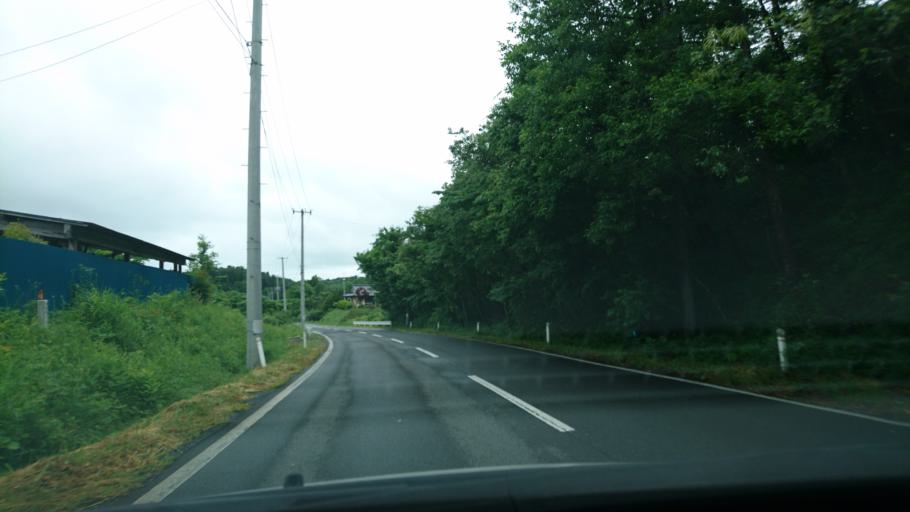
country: JP
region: Iwate
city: Ichinoseki
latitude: 38.8932
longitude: 141.1525
